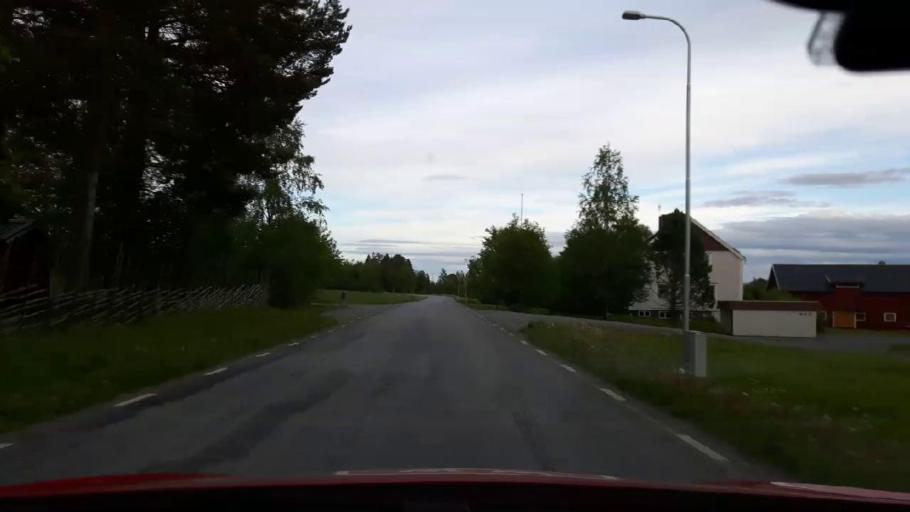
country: SE
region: Jaemtland
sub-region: Bergs Kommun
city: Hoverberg
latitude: 63.0242
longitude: 14.4757
